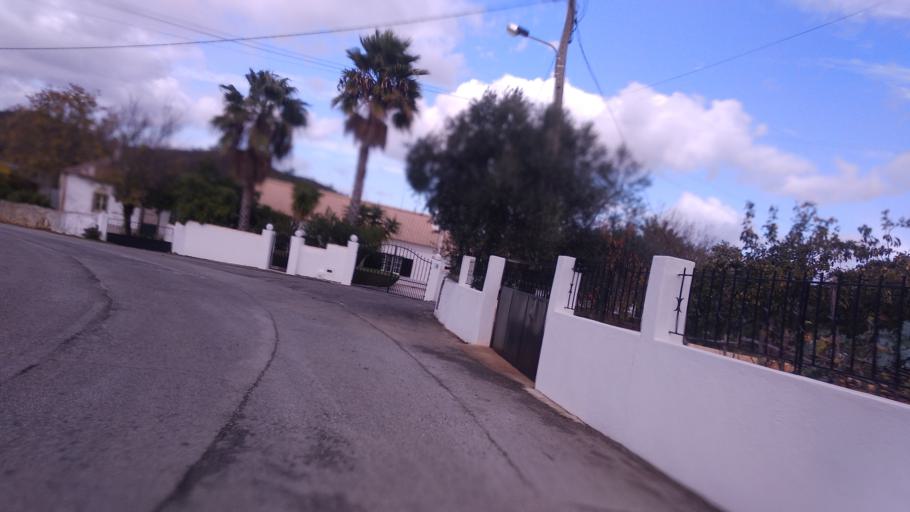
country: PT
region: Faro
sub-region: Sao Bras de Alportel
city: Sao Bras de Alportel
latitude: 37.1711
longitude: -7.8948
